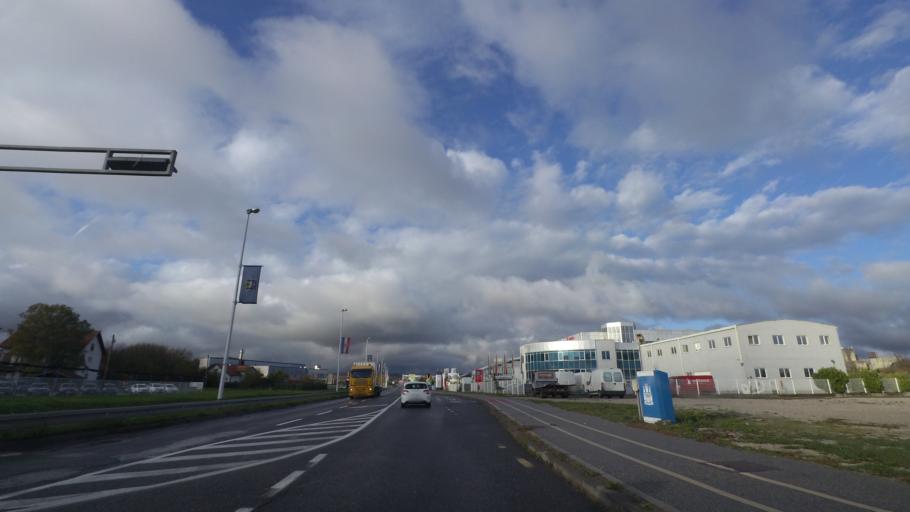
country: HR
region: Grad Zagreb
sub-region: Sesvete
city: Sesvete
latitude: 45.8172
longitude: 16.1019
